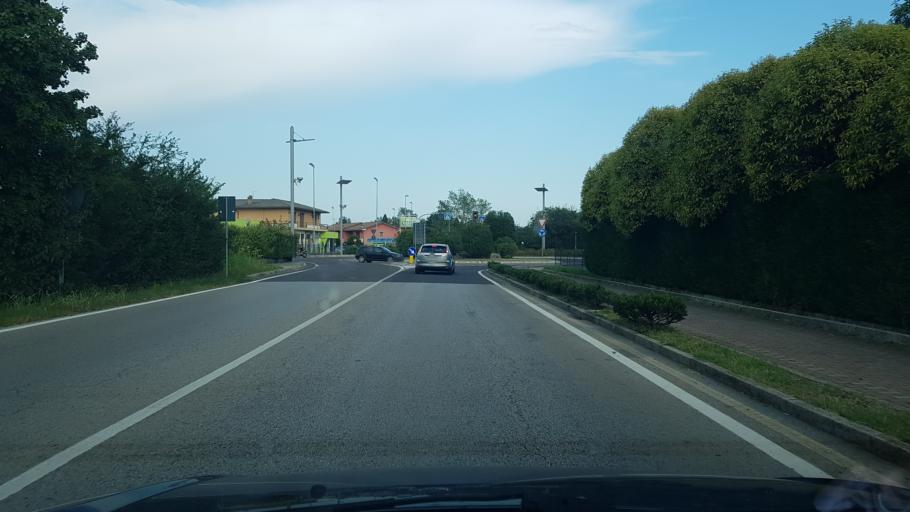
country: IT
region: Veneto
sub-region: Provincia di Vicenza
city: Marano Vicentino
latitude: 45.6984
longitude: 11.4398
